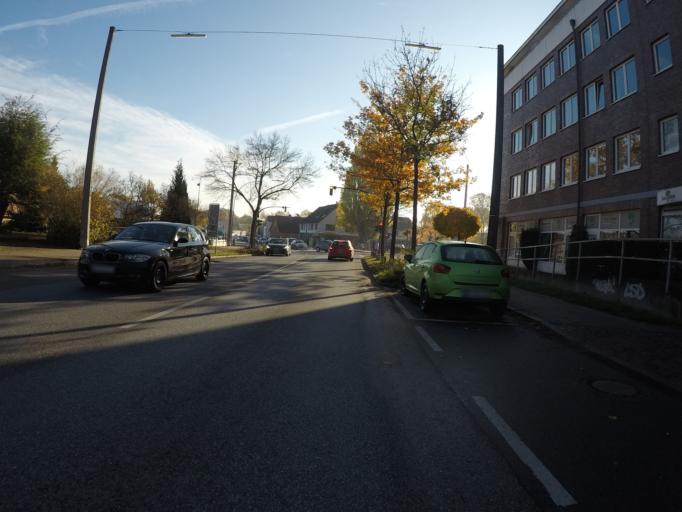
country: DE
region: Hamburg
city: Eidelstedt
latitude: 53.6297
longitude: 9.9280
